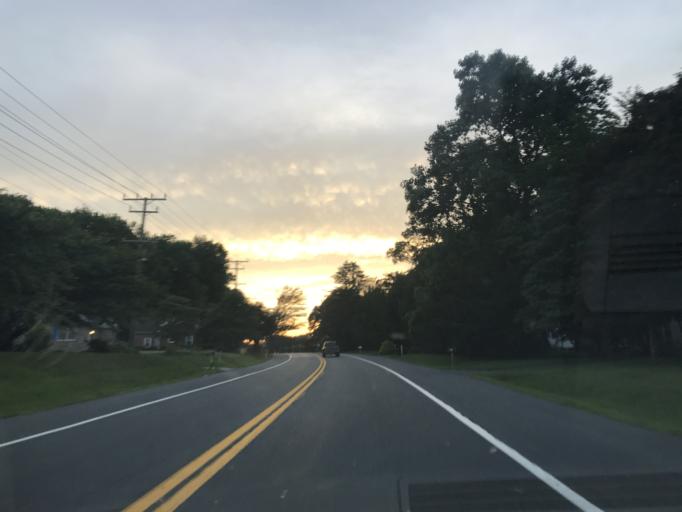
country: US
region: Maryland
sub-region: Harford County
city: Aberdeen
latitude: 39.5388
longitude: -76.2192
